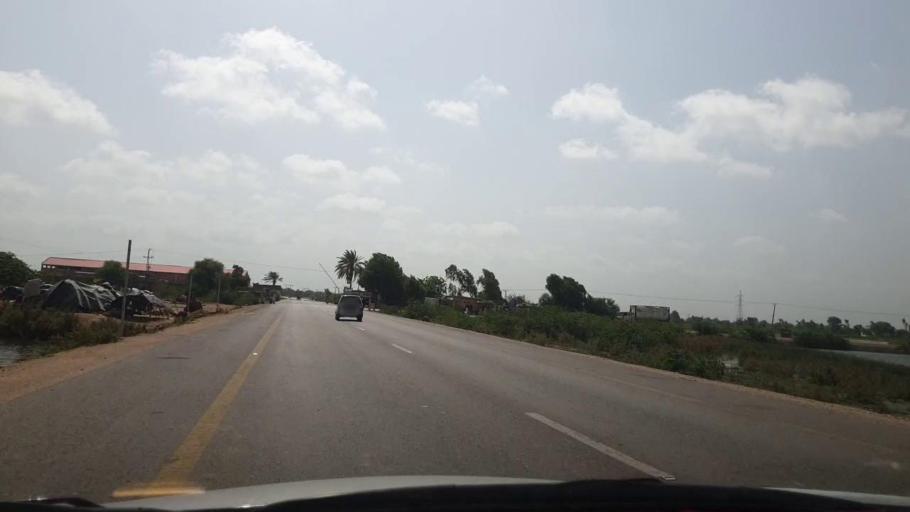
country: PK
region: Sindh
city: Talhar
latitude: 24.9140
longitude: 68.7295
